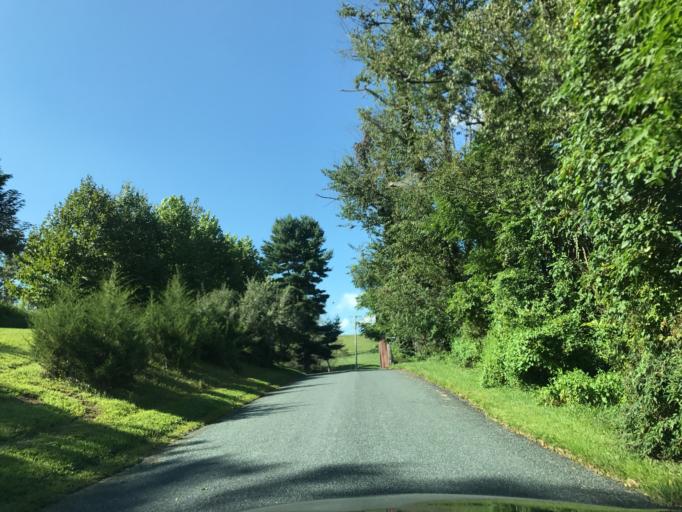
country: US
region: Pennsylvania
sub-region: York County
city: Stewartstown
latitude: 39.6956
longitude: -76.5572
